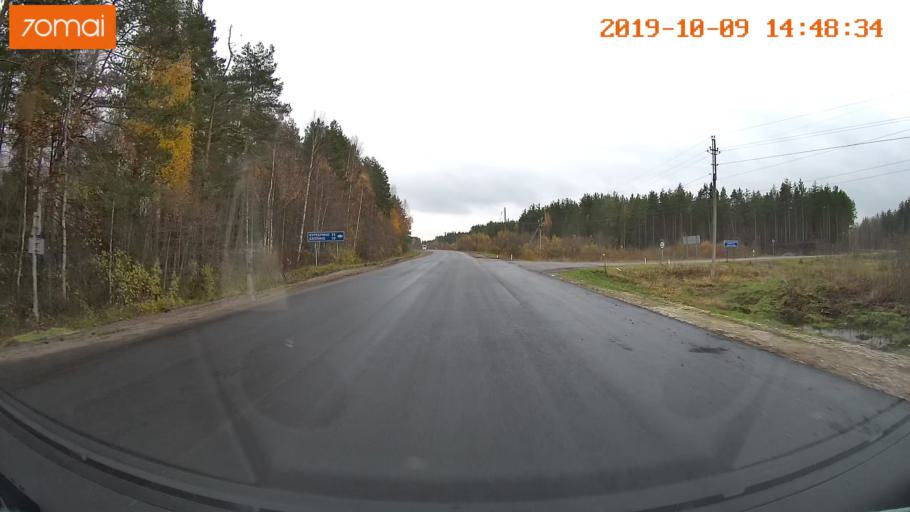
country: RU
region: Kostroma
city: Chistyye Bory
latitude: 58.4039
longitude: 41.5759
